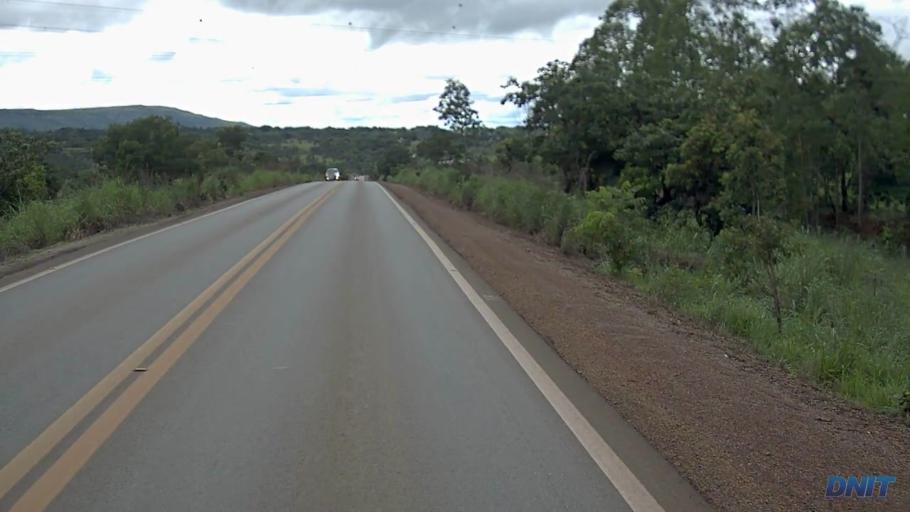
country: BR
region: Goias
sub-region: Padre Bernardo
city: Padre Bernardo
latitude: -15.3809
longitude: -48.2115
